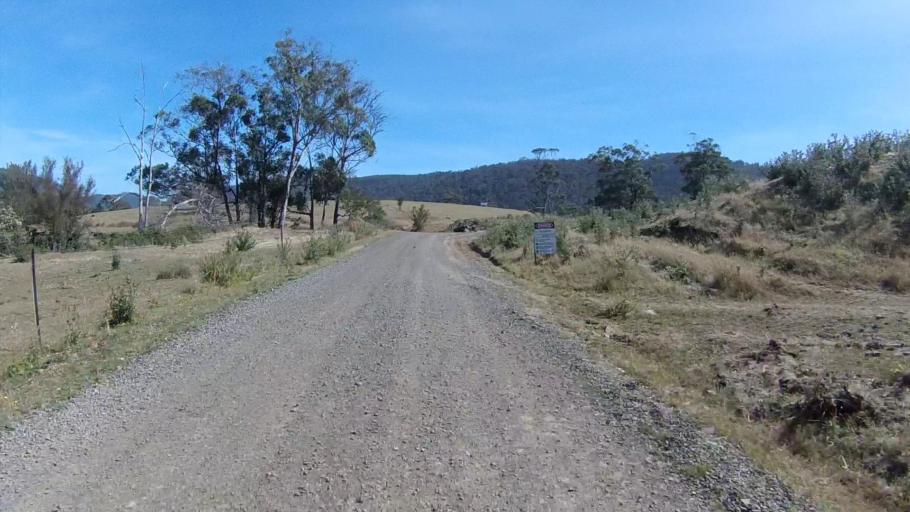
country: AU
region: Tasmania
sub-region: Sorell
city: Sorell
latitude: -42.7148
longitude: 147.5945
